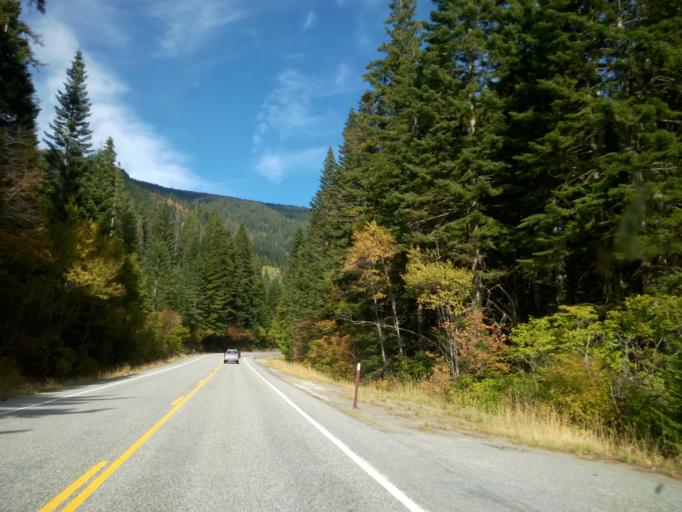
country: US
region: Washington
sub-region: Chelan County
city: Leavenworth
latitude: 47.7809
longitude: -120.9422
